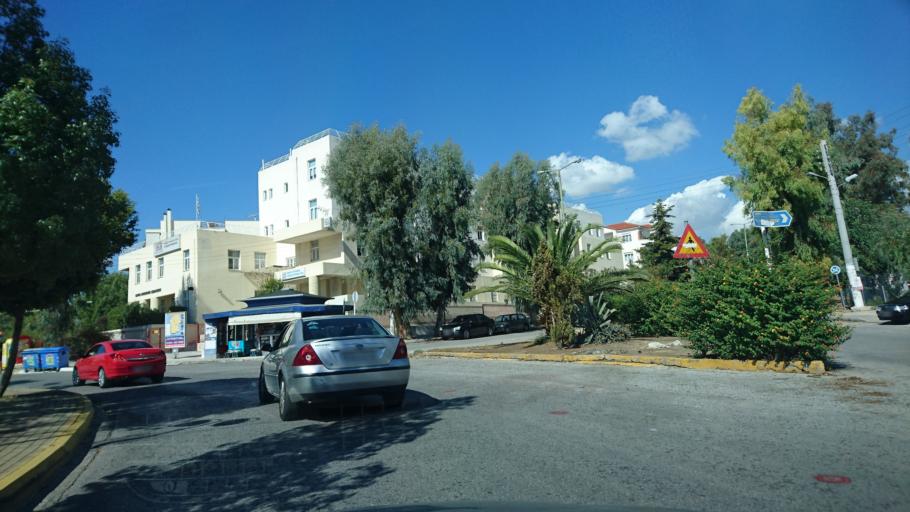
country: GR
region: Attica
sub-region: Nomarchia Athinas
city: Ymittos
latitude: 37.9375
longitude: 23.7523
